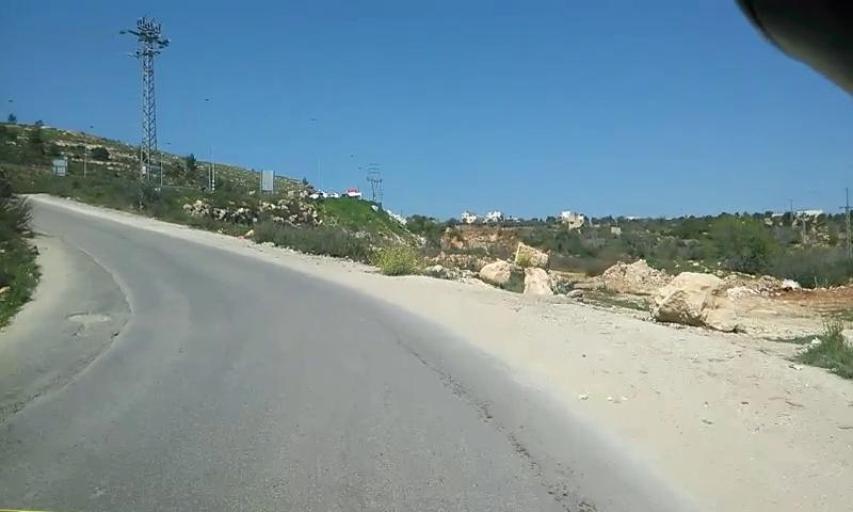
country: PS
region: West Bank
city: Al Khadir
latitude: 31.7048
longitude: 35.1572
